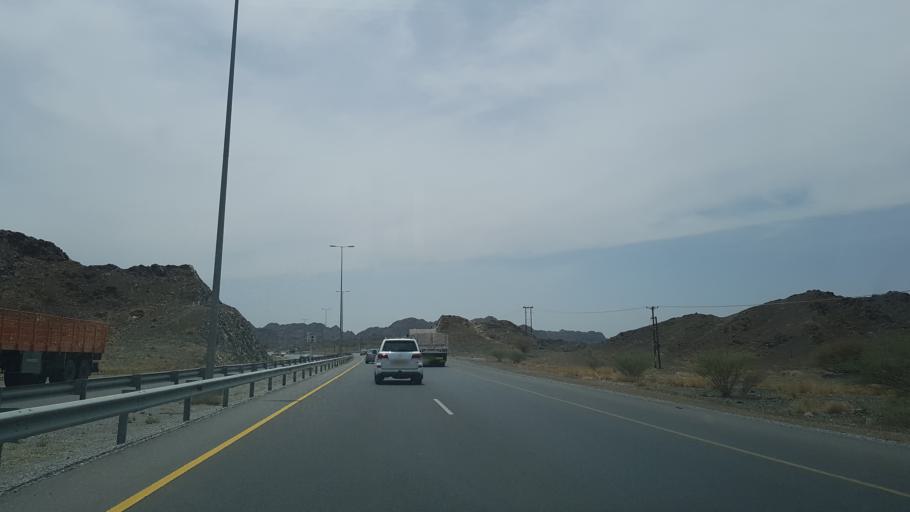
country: OM
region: Muhafazat ad Dakhiliyah
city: Izki
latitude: 22.9443
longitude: 57.7900
